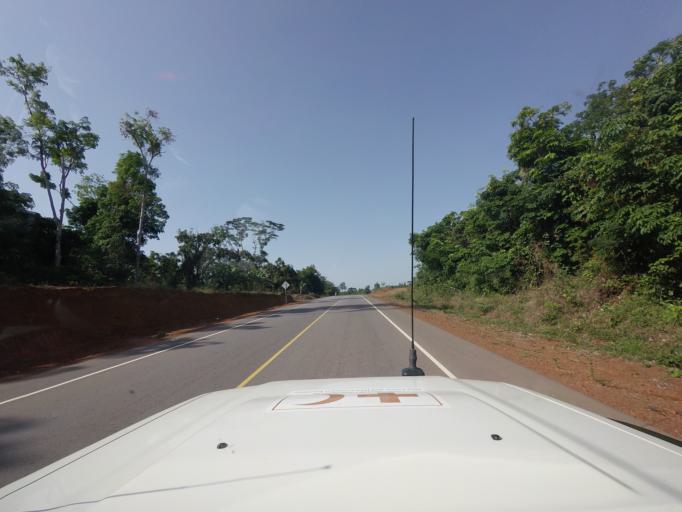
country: LR
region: Nimba
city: Sanniquellie
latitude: 7.1689
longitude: -9.0373
